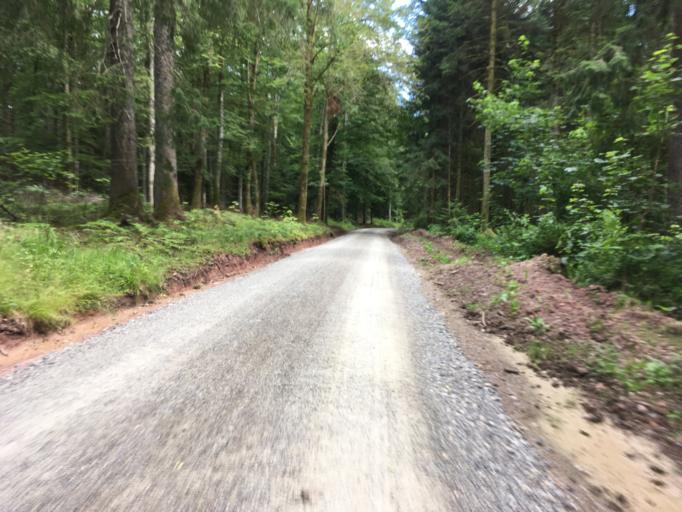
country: DE
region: Baden-Wuerttemberg
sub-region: Karlsruhe Region
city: Baiersbronn
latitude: 48.5459
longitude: 8.4232
